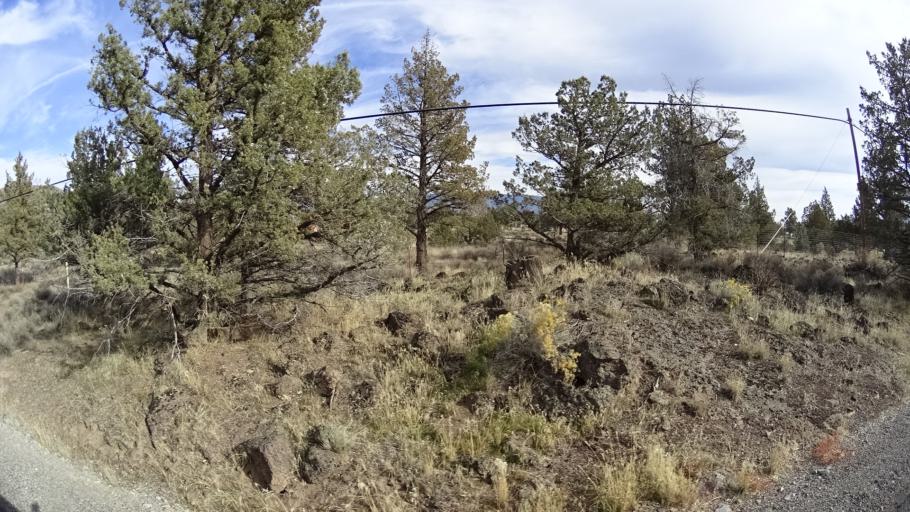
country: US
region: California
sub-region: Siskiyou County
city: Montague
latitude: 41.6546
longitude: -122.3995
